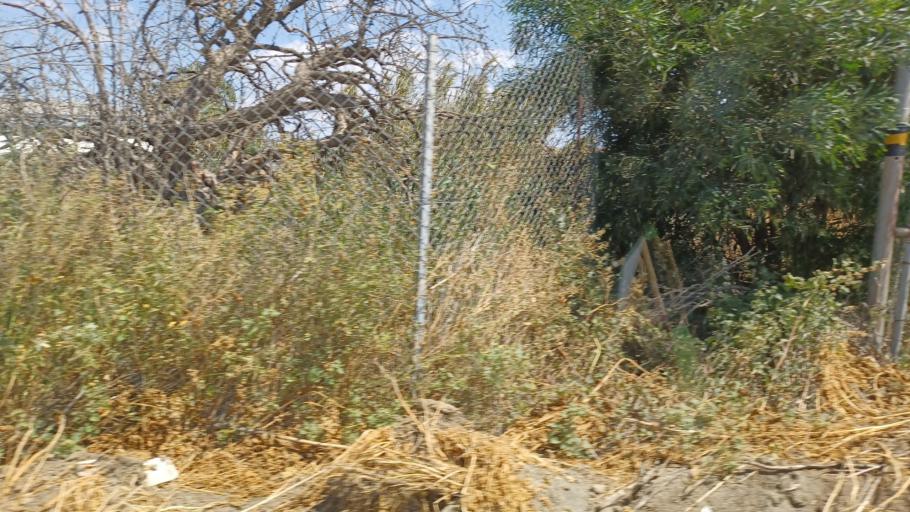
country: CY
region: Larnaka
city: Troulloi
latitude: 35.0174
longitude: 33.6106
